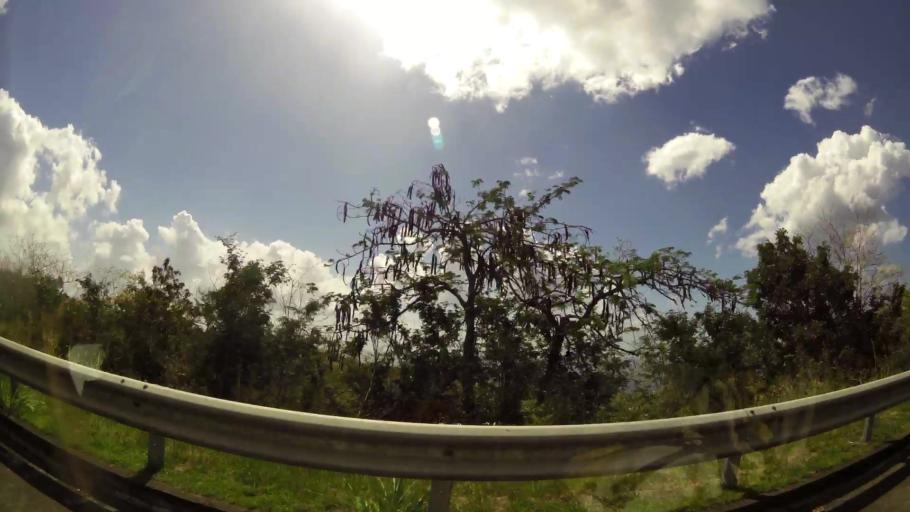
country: MQ
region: Martinique
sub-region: Martinique
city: Saint-Pierre
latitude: 14.6951
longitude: -61.1673
